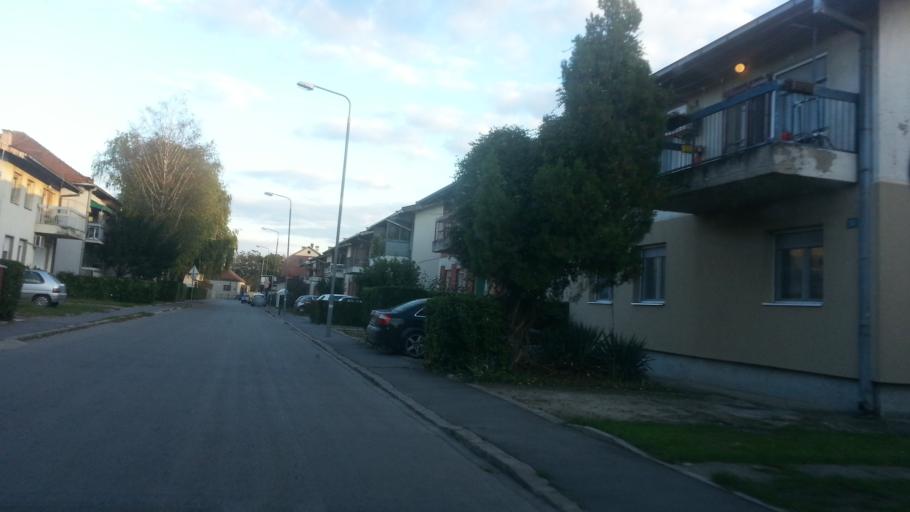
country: RS
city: Novi Banovci
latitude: 44.8993
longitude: 20.2896
